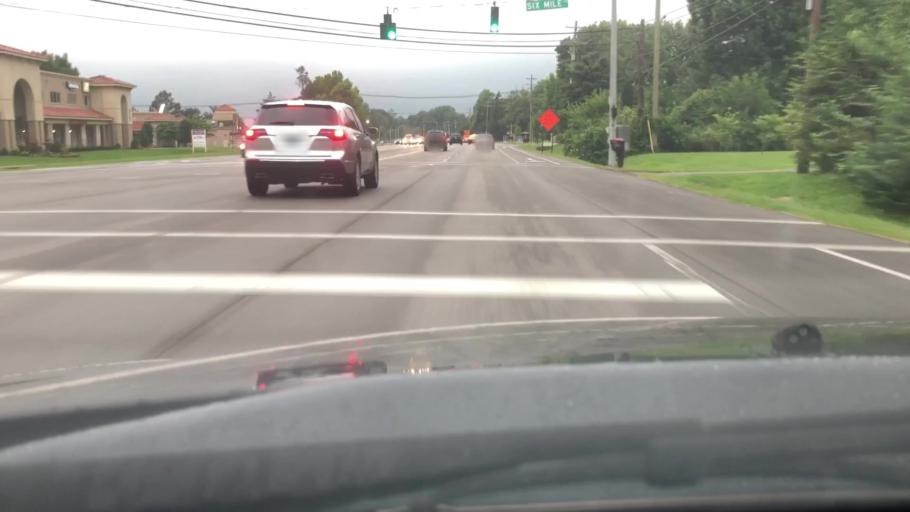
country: US
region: Kentucky
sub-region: Jefferson County
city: Hurstbourne Acres
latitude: 38.2114
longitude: -85.5864
